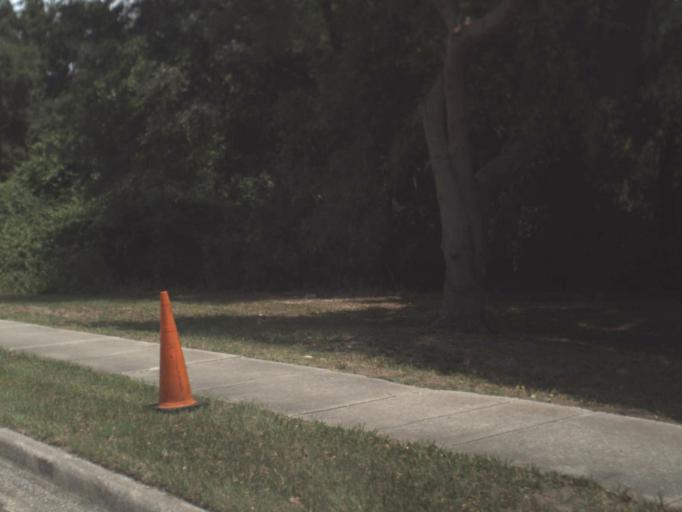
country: US
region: Florida
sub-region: Nassau County
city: Fernandina Beach
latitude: 30.6507
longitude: -81.4601
